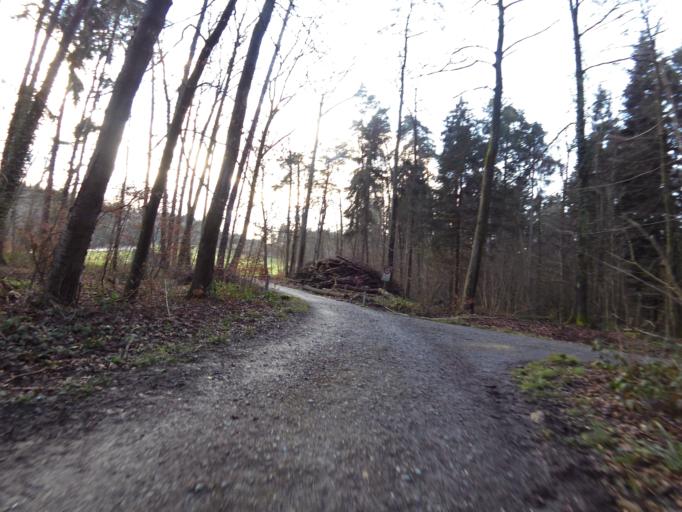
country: CH
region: Zurich
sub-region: Bezirk Zuerich
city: Zuerich (Kreis 9)
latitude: 47.3757
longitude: 8.4753
